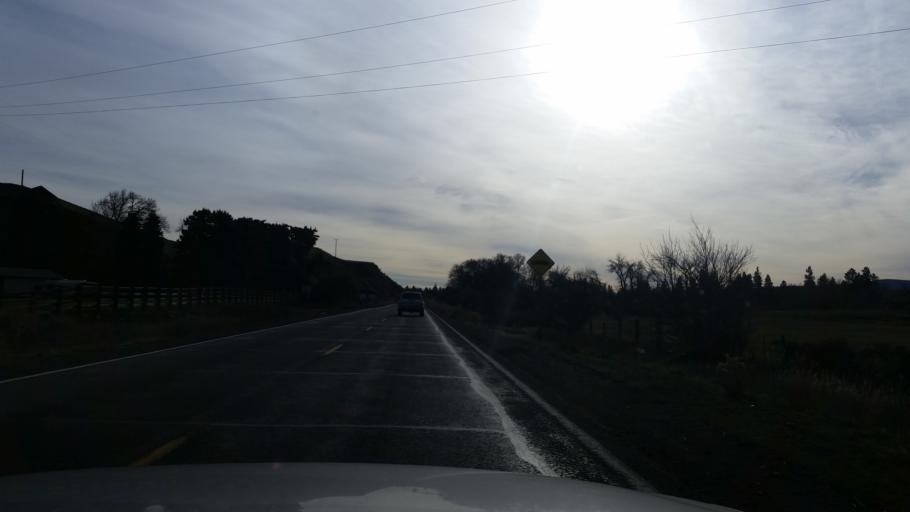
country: US
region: Washington
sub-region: Kittitas County
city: Ellensburg
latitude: 47.0839
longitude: -120.6756
